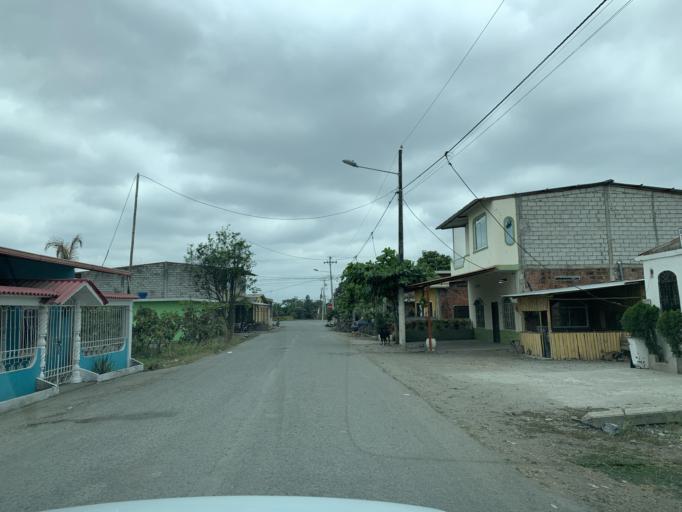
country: EC
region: Guayas
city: Coronel Marcelino Mariduena
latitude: -2.3175
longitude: -79.4695
